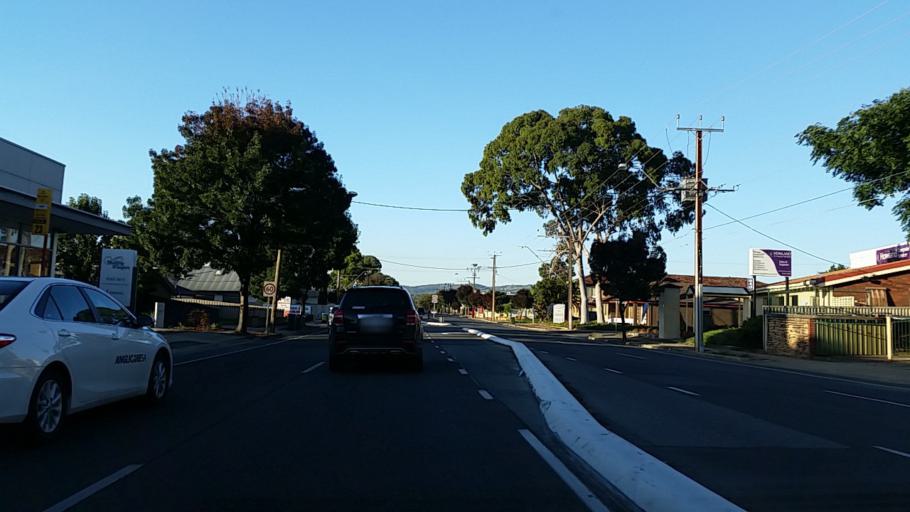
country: AU
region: South Australia
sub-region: Campbelltown
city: Paradise
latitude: -34.8759
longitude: 138.6657
